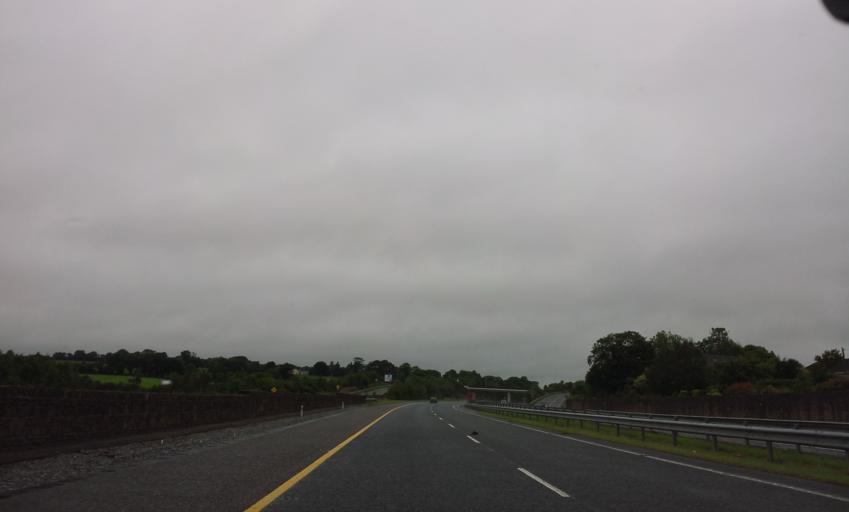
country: IE
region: Munster
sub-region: County Cork
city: Watergrasshill
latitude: 51.9510
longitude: -8.3906
